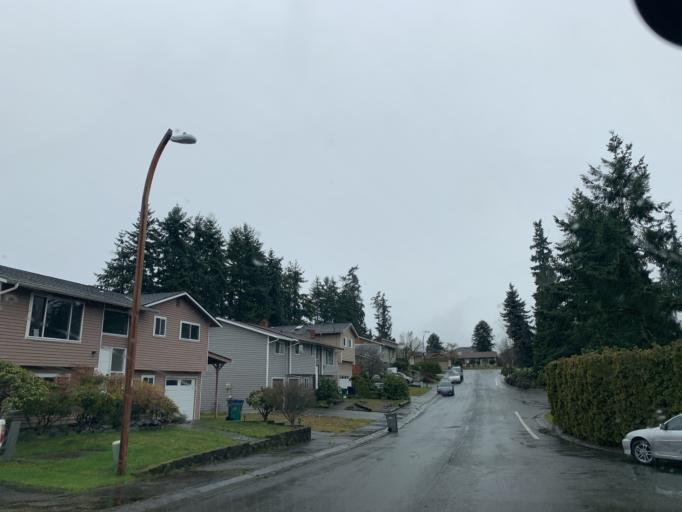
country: US
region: Washington
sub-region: King County
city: Kingsgate
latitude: 47.7397
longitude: -122.1716
